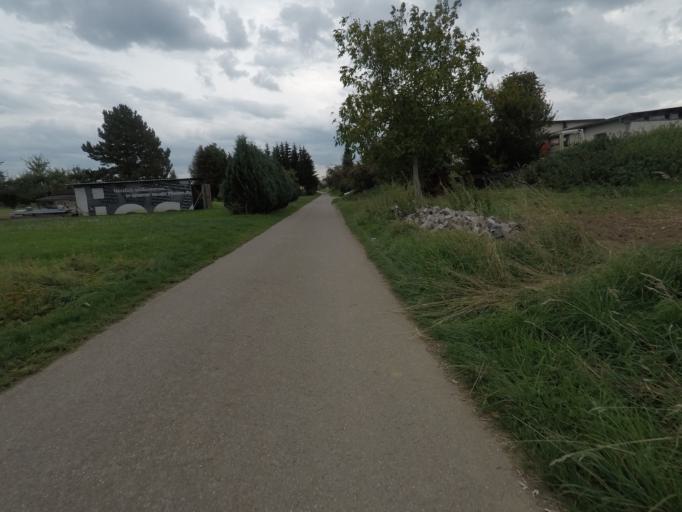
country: DE
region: Baden-Wuerttemberg
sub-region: Regierungsbezirk Stuttgart
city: Herrenberg
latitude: 48.5620
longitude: 8.8994
